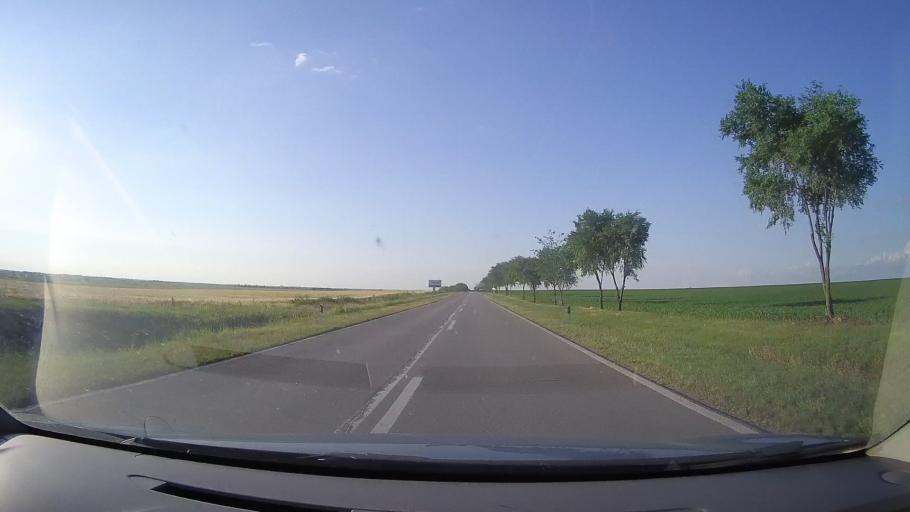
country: RO
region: Timis
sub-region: Comuna Moravita
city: Moravita
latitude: 45.1970
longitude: 21.3000
